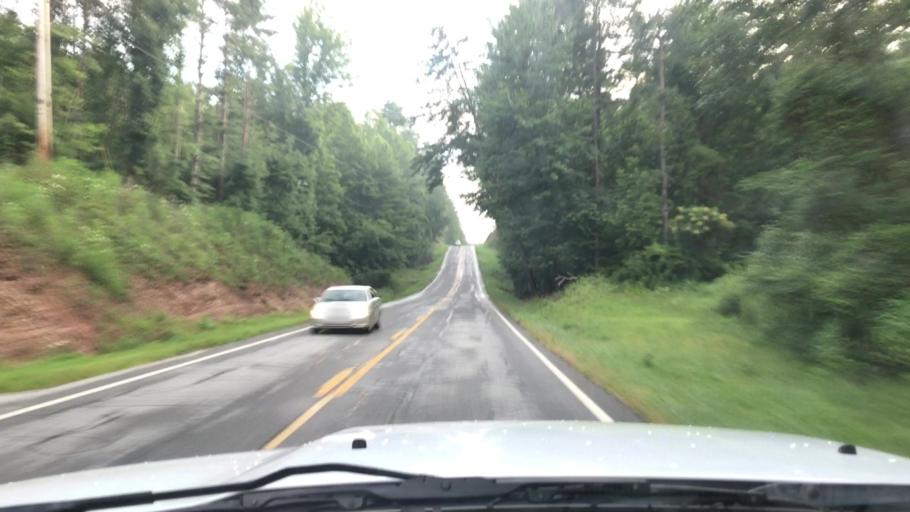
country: US
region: Georgia
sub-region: Fannin County
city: Blue Ridge
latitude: 34.9449
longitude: -84.2433
